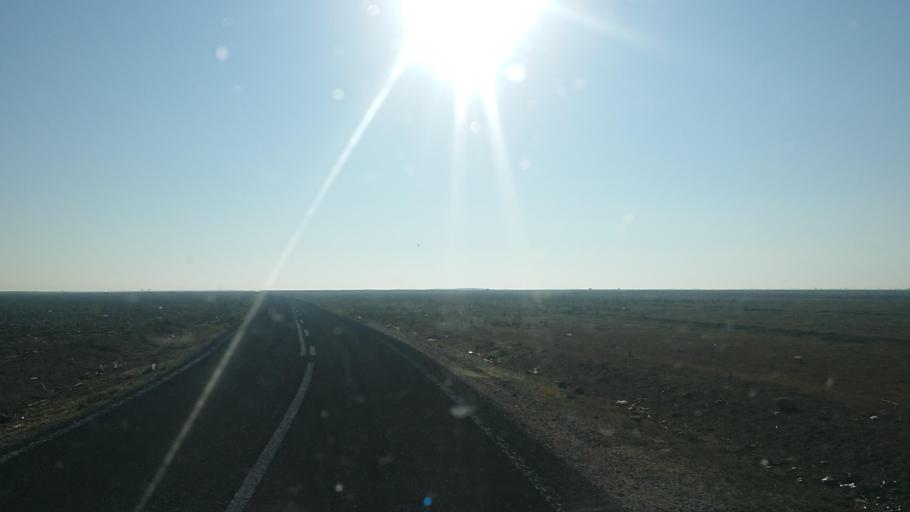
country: TR
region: Aksaray
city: Yesilova
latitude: 38.3880
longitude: 33.7489
